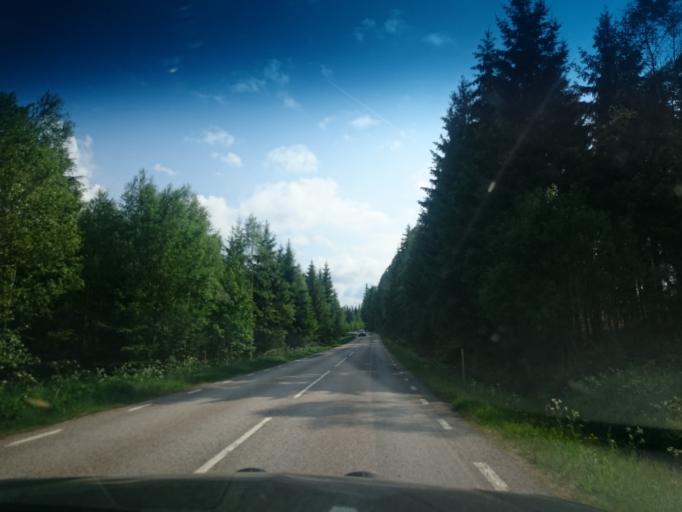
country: SE
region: Joenkoeping
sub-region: Vetlanda Kommun
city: Vetlanda
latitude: 57.3500
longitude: 15.0730
